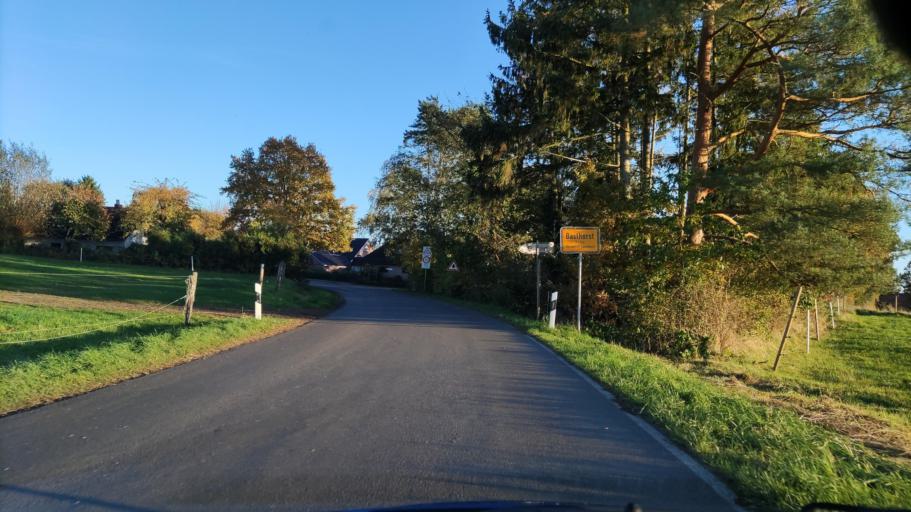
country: DE
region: Schleswig-Holstein
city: Basthorst
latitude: 53.5786
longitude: 10.4679
